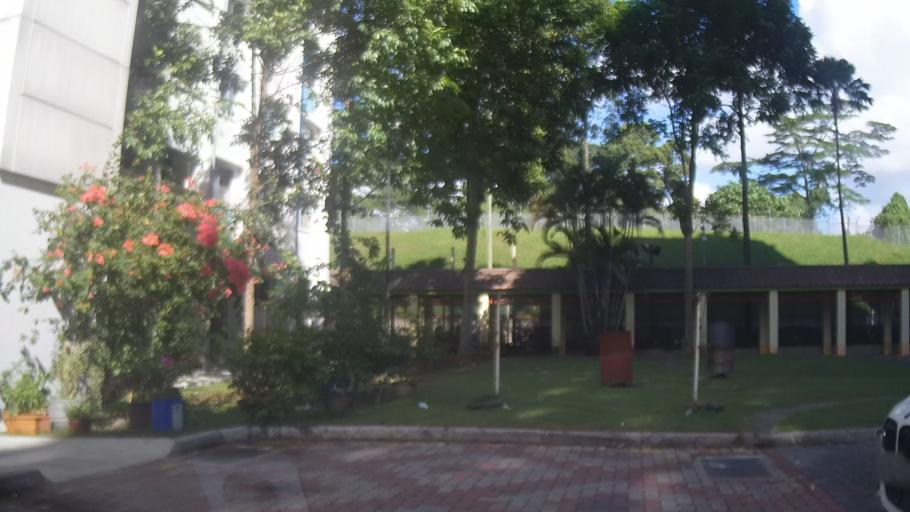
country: MY
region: Johor
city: Johor Bahru
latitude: 1.4273
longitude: 103.7724
